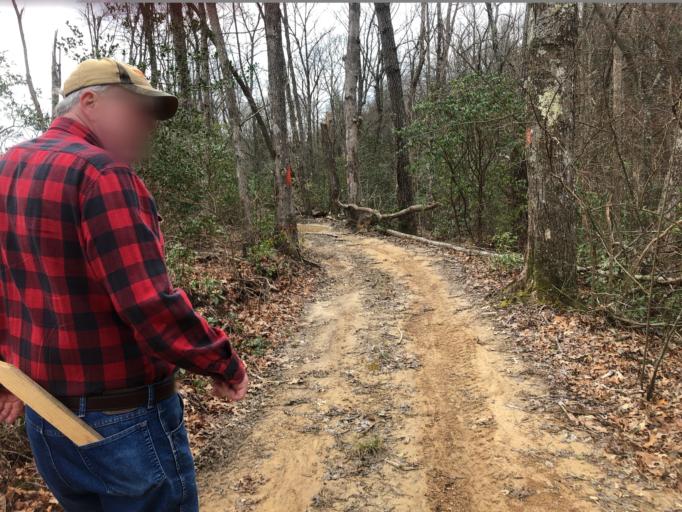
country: US
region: Tennessee
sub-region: Cumberland County
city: Fairfield Glade
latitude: 35.9703
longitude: -84.7670
